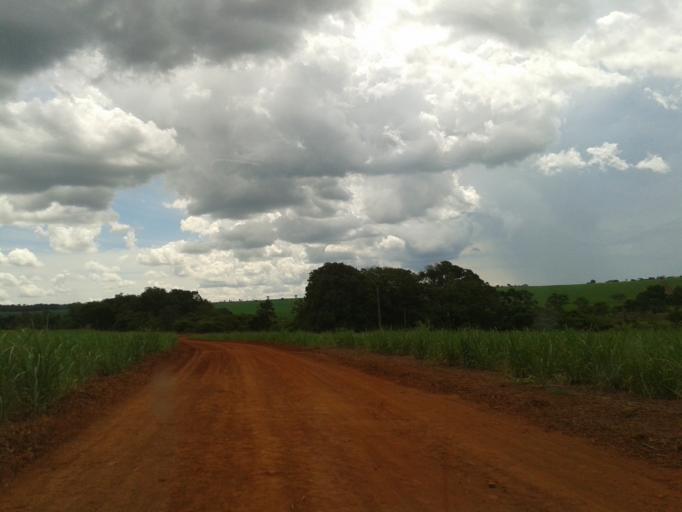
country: BR
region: Minas Gerais
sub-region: Centralina
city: Centralina
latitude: -18.6650
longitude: -49.2339
